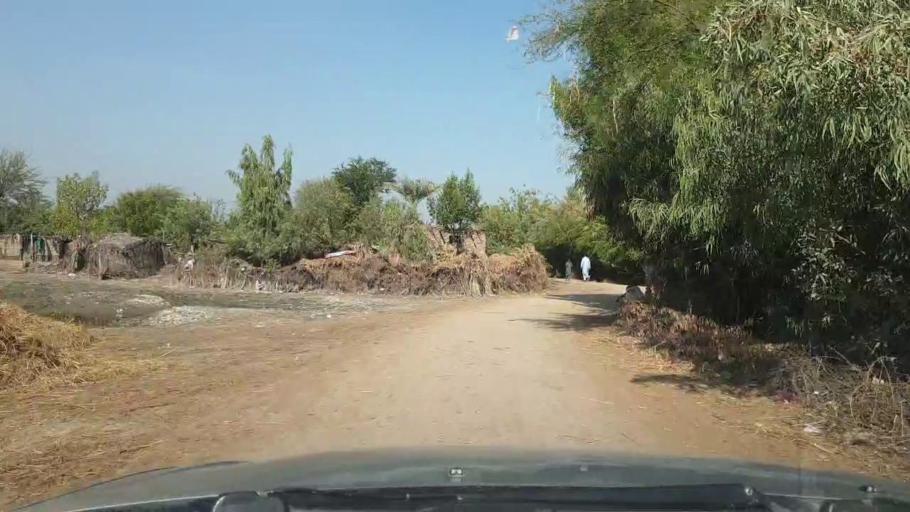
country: PK
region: Sindh
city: Tando Muhammad Khan
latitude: 25.1408
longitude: 68.5356
